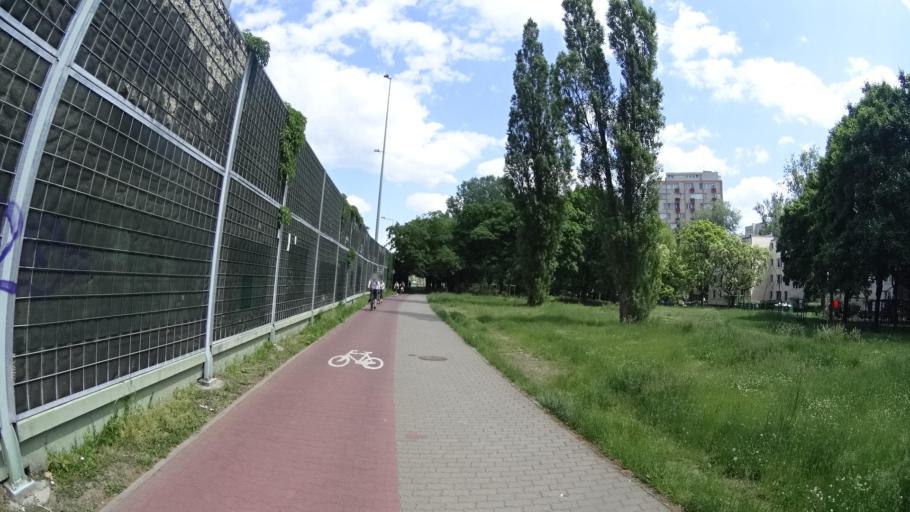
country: PL
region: Masovian Voivodeship
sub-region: Warszawa
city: Praga Polnoc
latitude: 52.2649
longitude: 21.0256
